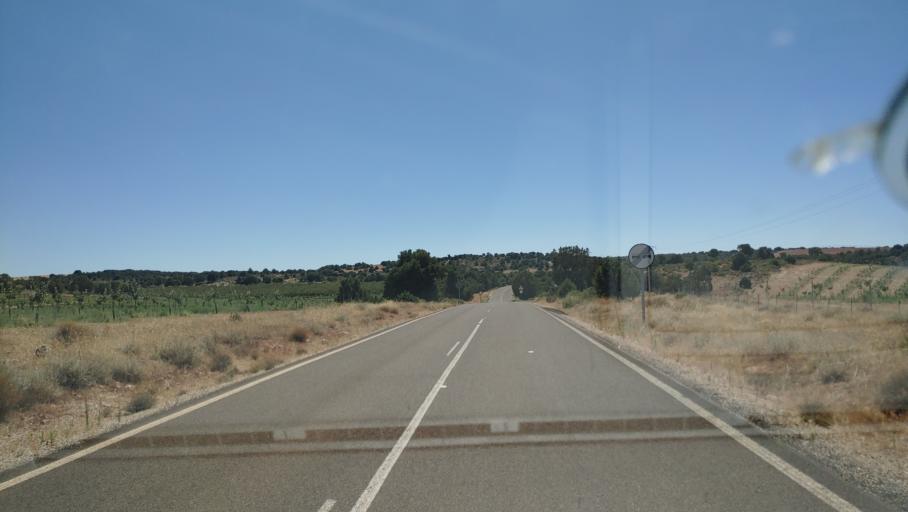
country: ES
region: Castille-La Mancha
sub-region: Provincia de Albacete
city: Ossa de Montiel
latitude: 38.8559
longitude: -2.8024
